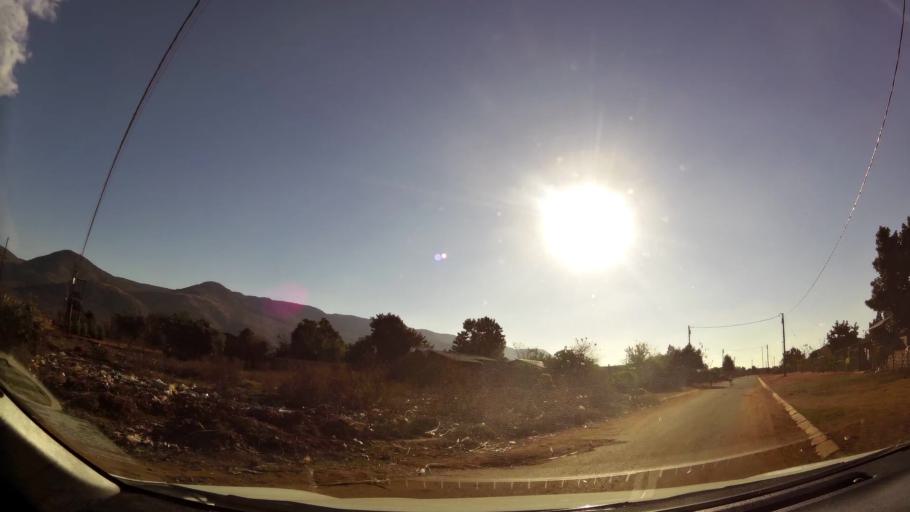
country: ZA
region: Limpopo
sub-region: Waterberg District Municipality
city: Mokopane
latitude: -24.1870
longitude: 28.9735
